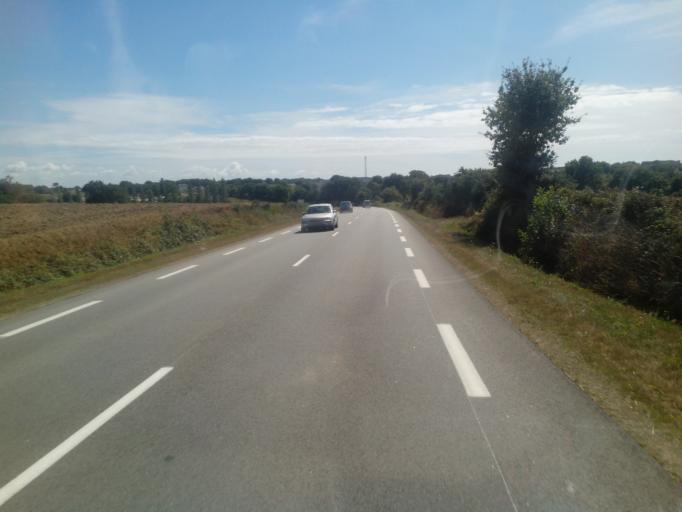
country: FR
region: Brittany
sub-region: Departement du Morbihan
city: Peaule
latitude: 47.5452
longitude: -2.3992
